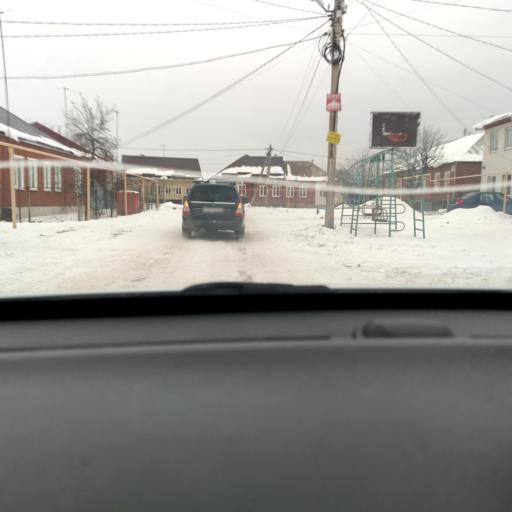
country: RU
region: Voronezj
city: Somovo
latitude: 51.7499
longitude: 39.3412
